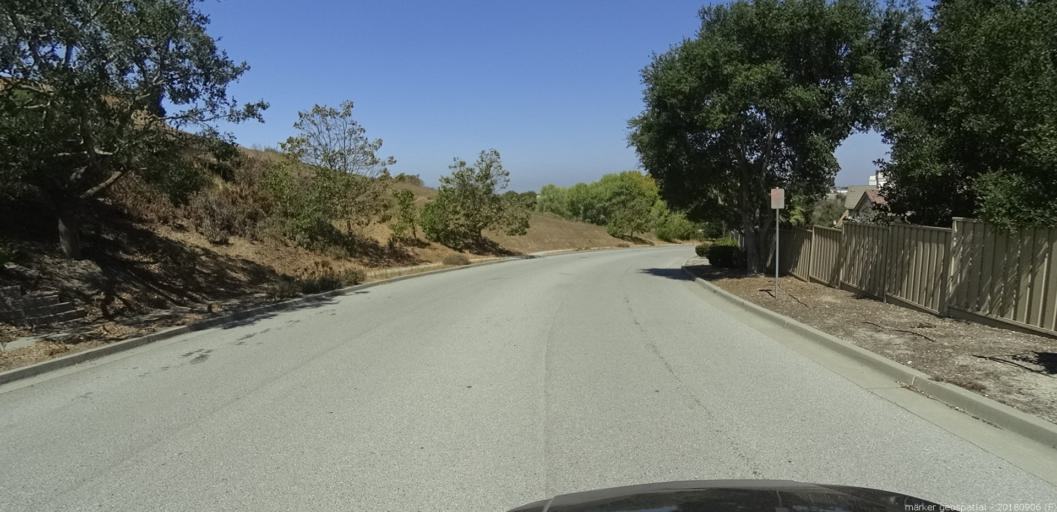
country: US
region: California
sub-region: Monterey County
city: Salinas
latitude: 36.6080
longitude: -121.6496
